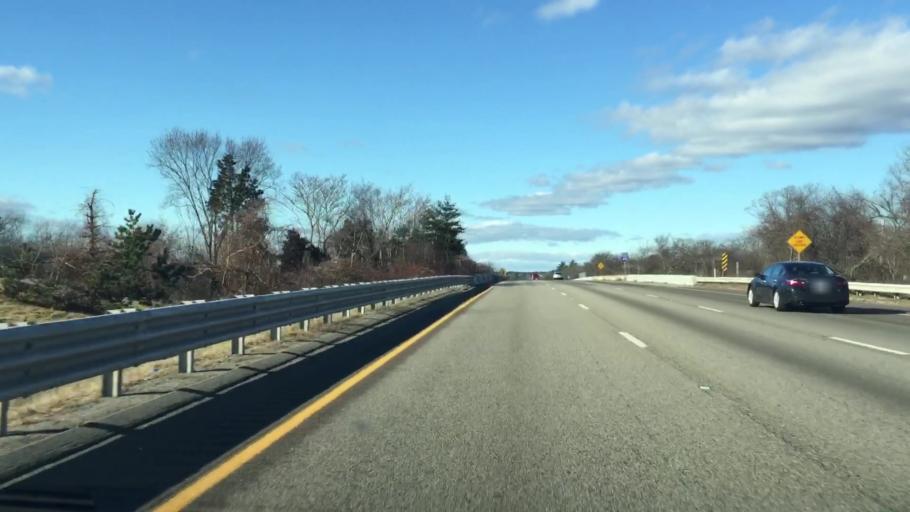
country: US
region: Massachusetts
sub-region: Bristol County
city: Mansfield Center
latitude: 42.0120
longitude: -71.2321
